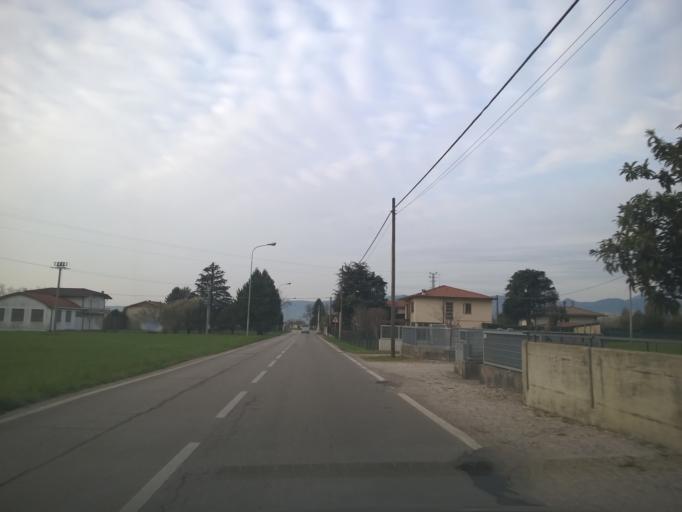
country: IT
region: Veneto
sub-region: Provincia di Vicenza
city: Zane
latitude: 45.7114
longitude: 11.4535
